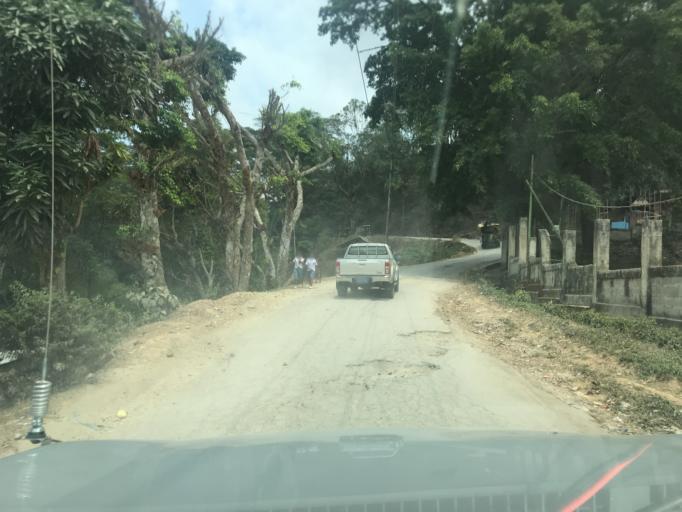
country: TL
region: Dili
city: Dili
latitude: -8.6015
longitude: 125.5951
